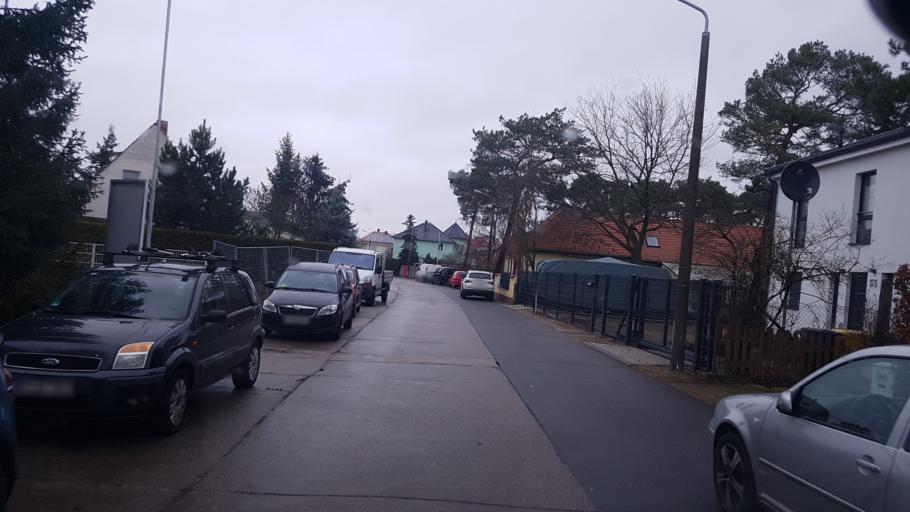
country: DE
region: Berlin
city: Wannsee
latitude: 52.3575
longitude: 13.1300
